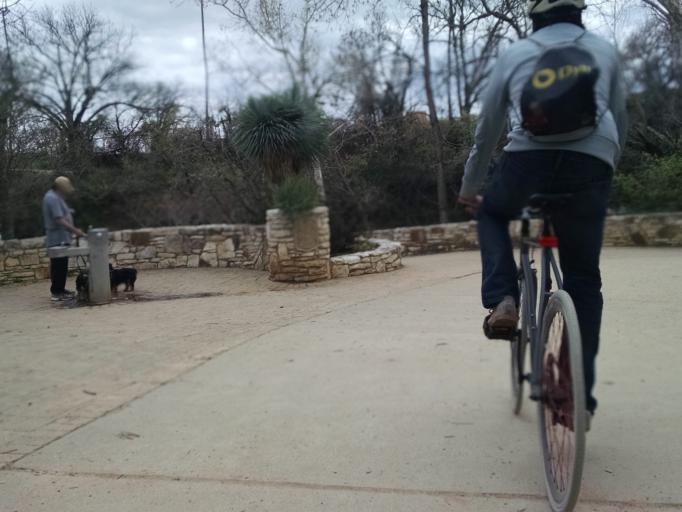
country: US
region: Texas
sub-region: Travis County
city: Austin
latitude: 30.2672
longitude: -97.7620
